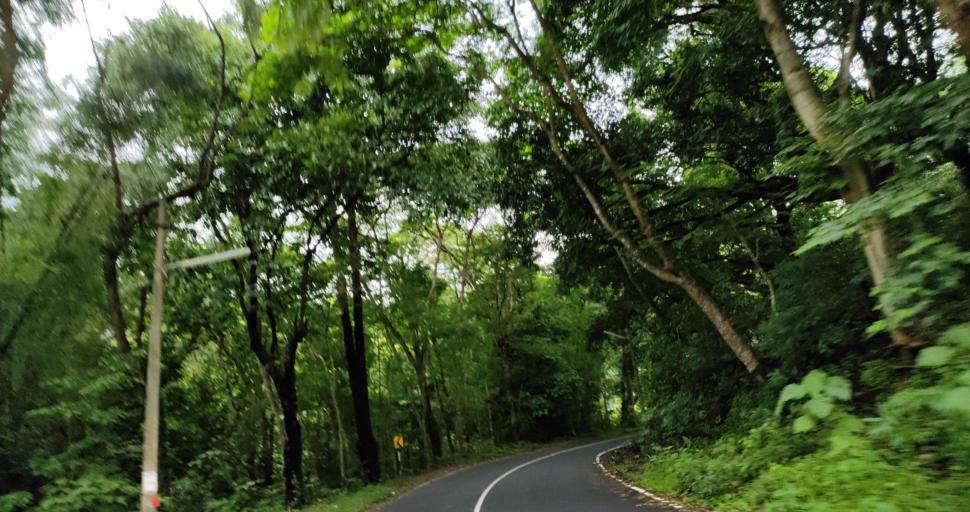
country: IN
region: Kerala
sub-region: Ernakulam
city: Angamali
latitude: 10.2992
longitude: 76.4533
